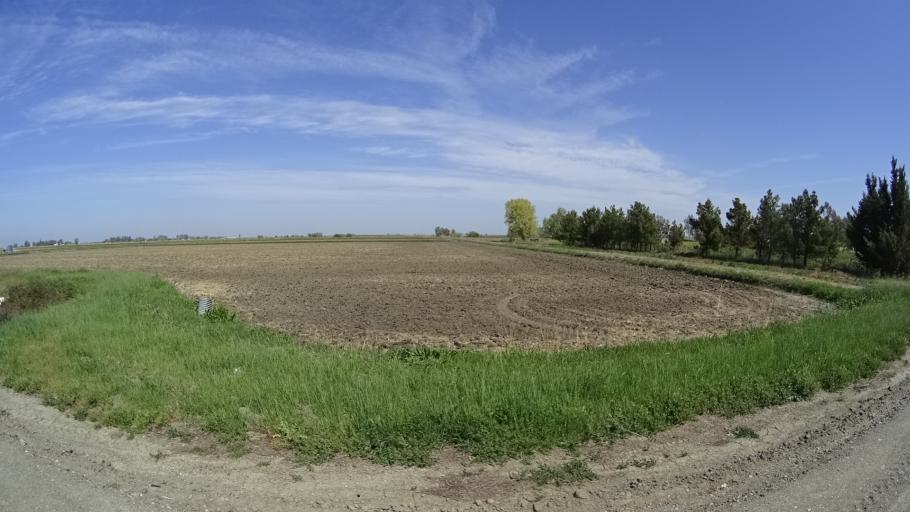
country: US
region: California
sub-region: Glenn County
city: Hamilton City
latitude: 39.5824
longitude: -122.0396
